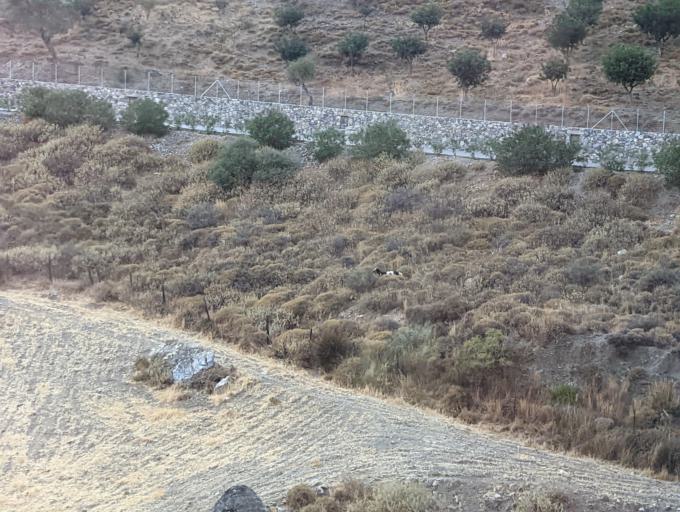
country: GR
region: Crete
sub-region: Nomos Rethymnis
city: Atsipopoulon
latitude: 35.1582
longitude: 24.4589
